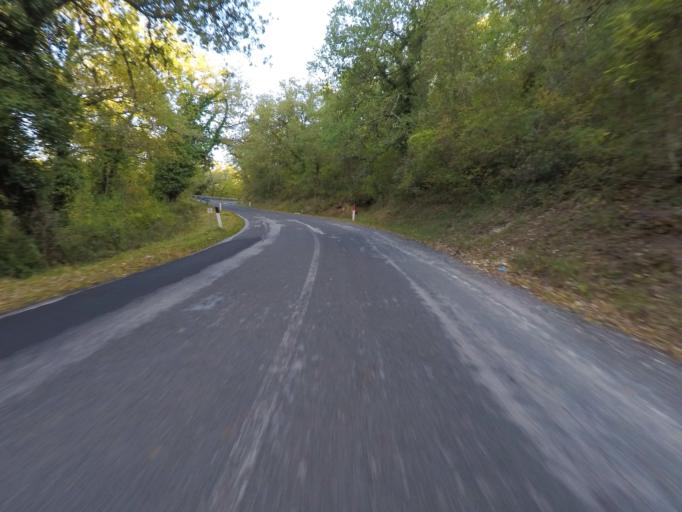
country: IT
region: Tuscany
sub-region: Provincia di Siena
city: Radda in Chianti
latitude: 43.4640
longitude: 11.3829
